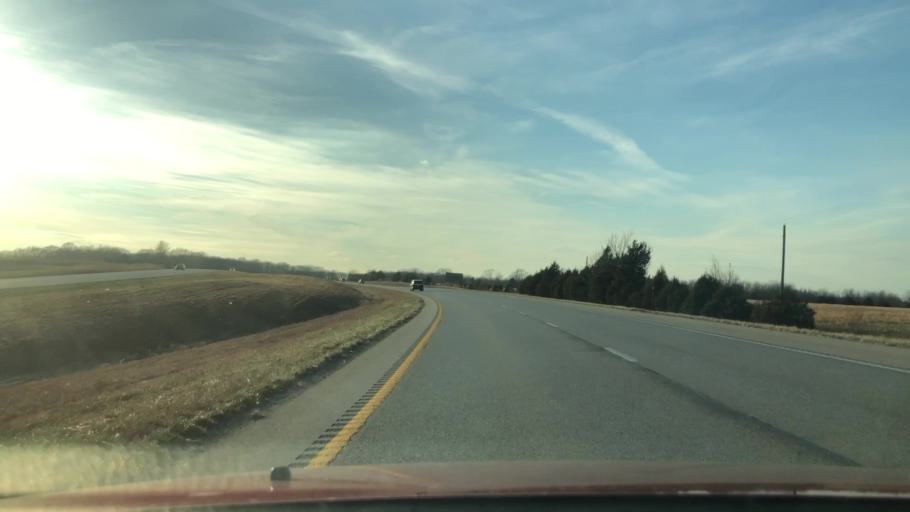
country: US
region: Missouri
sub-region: Webster County
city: Seymour
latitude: 37.1314
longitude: -92.7232
